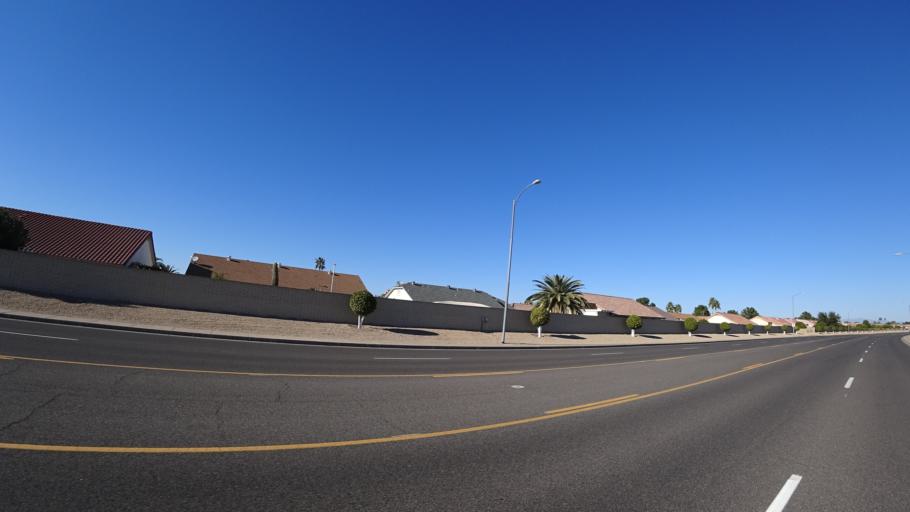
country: US
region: Arizona
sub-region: Maricopa County
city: Sun City West
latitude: 33.6733
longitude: -112.3696
